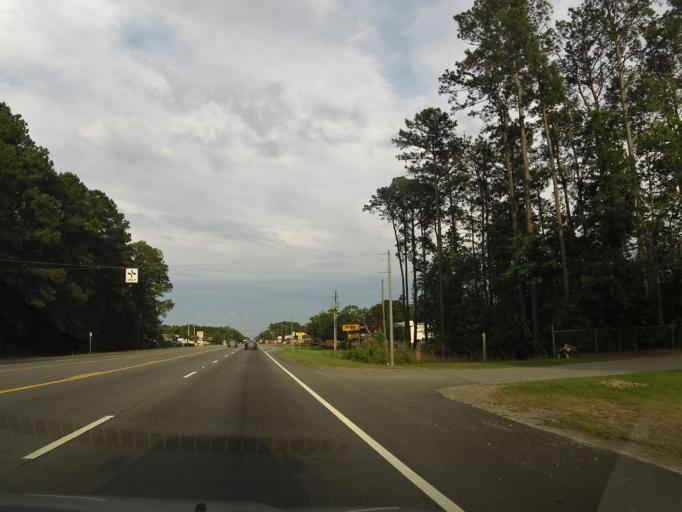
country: US
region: Georgia
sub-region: Chatham County
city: Pooler
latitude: 32.0947
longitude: -81.2066
